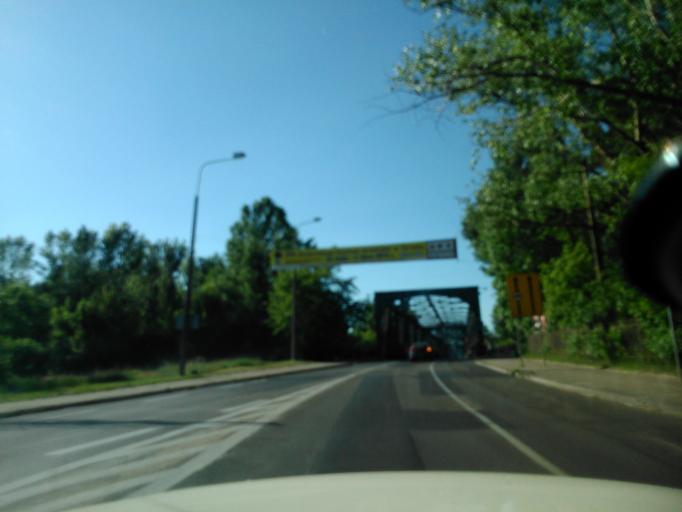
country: PL
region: Kujawsko-Pomorskie
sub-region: Torun
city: Torun
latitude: 52.9994
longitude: 18.6050
